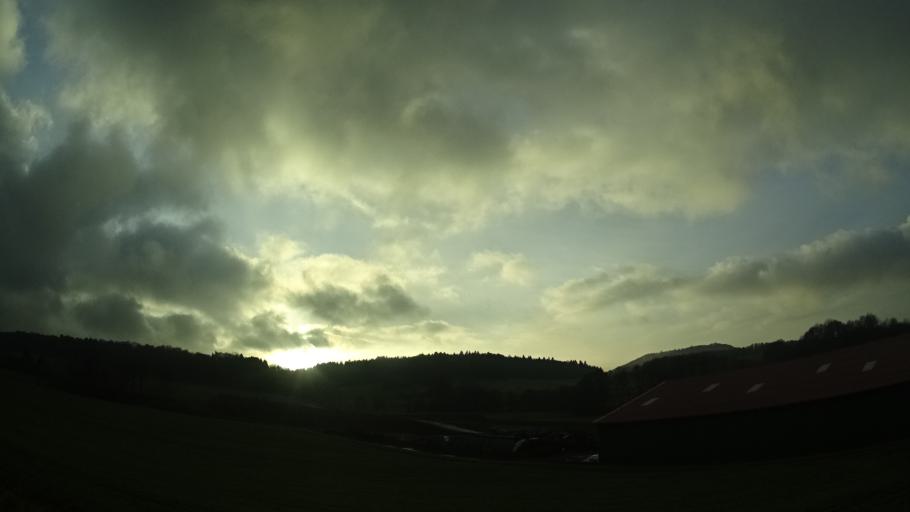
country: DE
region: Hesse
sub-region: Regierungsbezirk Kassel
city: Hofbieber
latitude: 50.5625
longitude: 9.8720
